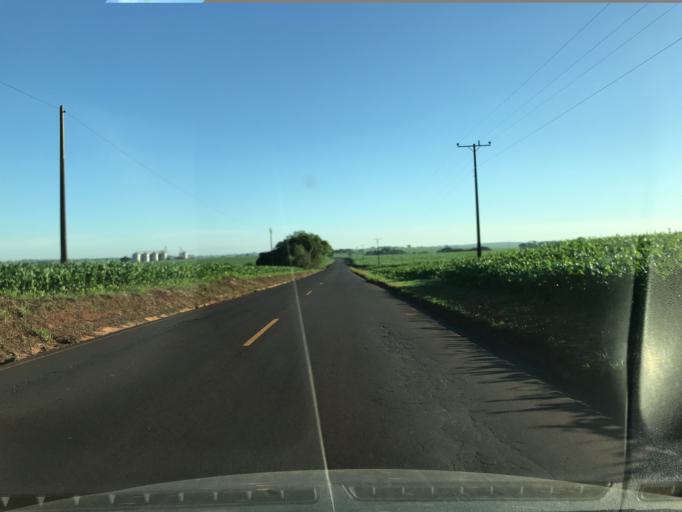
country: BR
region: Parana
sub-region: Palotina
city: Palotina
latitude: -24.1300
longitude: -53.8528
